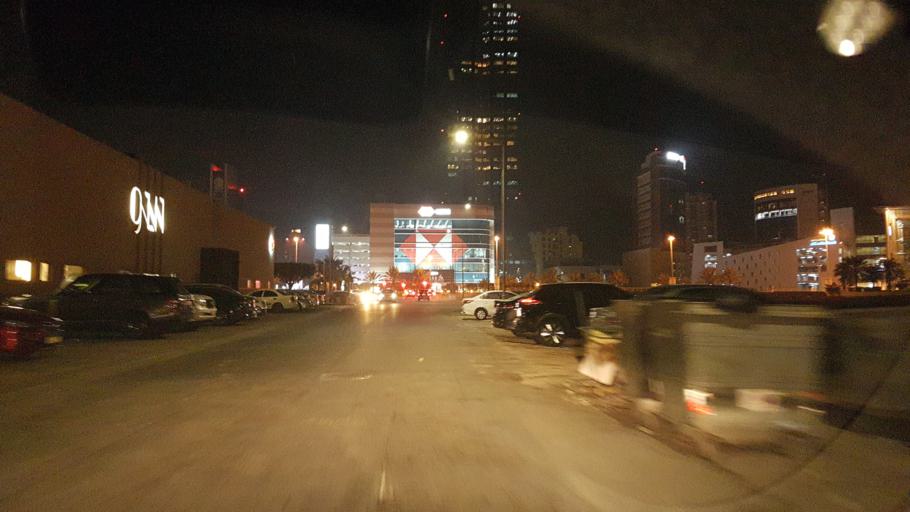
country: BH
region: Manama
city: Jidd Hafs
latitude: 26.2329
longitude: 50.5415
